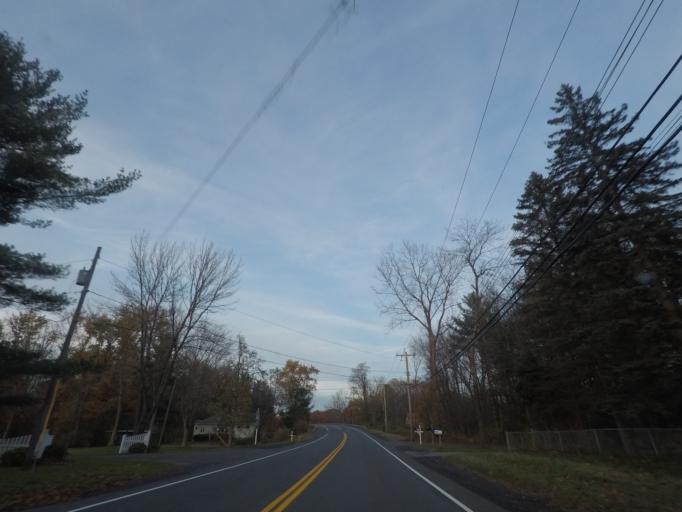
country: US
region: New York
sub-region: Schenectady County
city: Rotterdam
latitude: 42.7690
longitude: -73.9773
